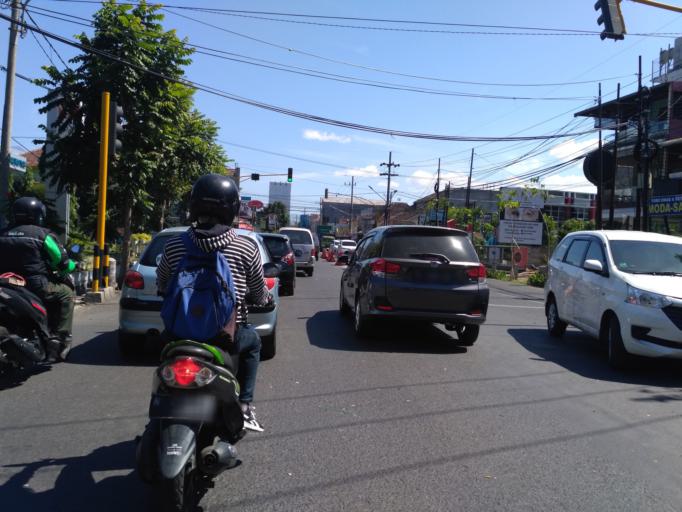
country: ID
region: East Java
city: Malang
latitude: -7.9812
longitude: 112.6540
